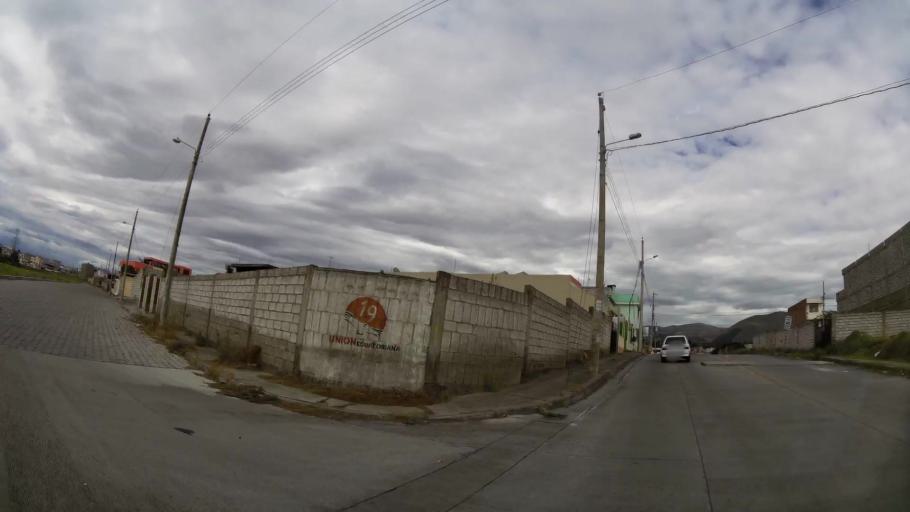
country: EC
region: Cotopaxi
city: Latacunga
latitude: -0.9507
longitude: -78.6177
